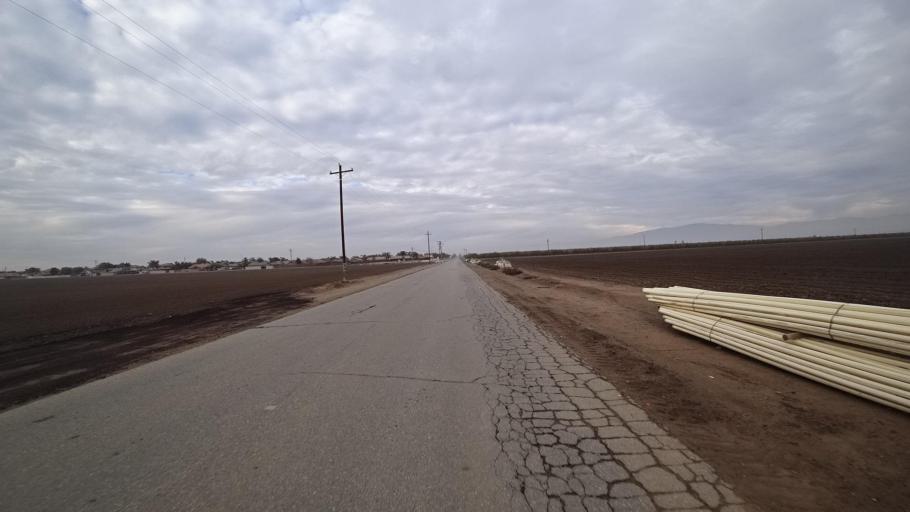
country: US
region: California
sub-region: Kern County
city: Arvin
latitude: 35.1855
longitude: -118.8241
